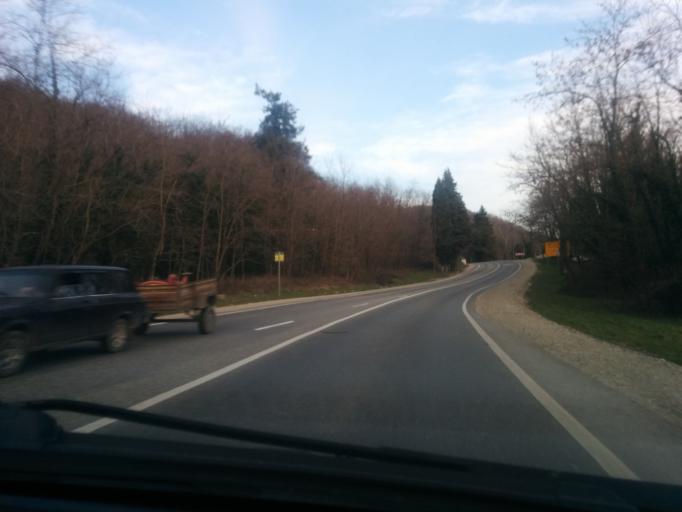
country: RU
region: Krasnodarskiy
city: Nebug
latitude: 44.1742
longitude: 38.9659
